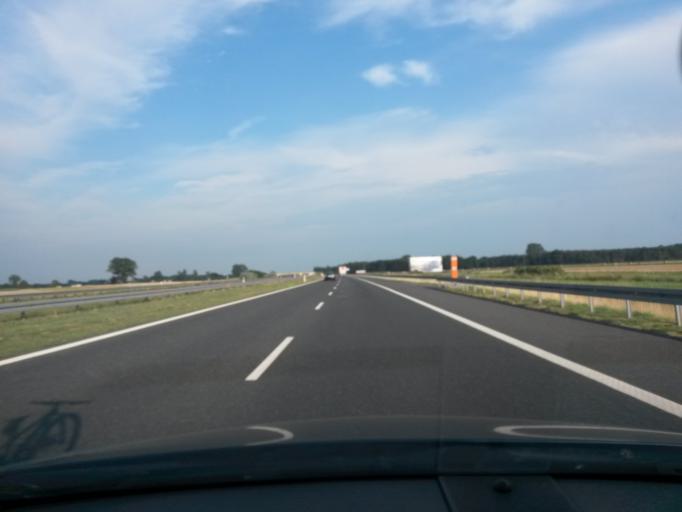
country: PL
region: Lodz Voivodeship
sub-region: Powiat poddebicki
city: Dalikow
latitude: 51.9571
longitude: 19.1325
